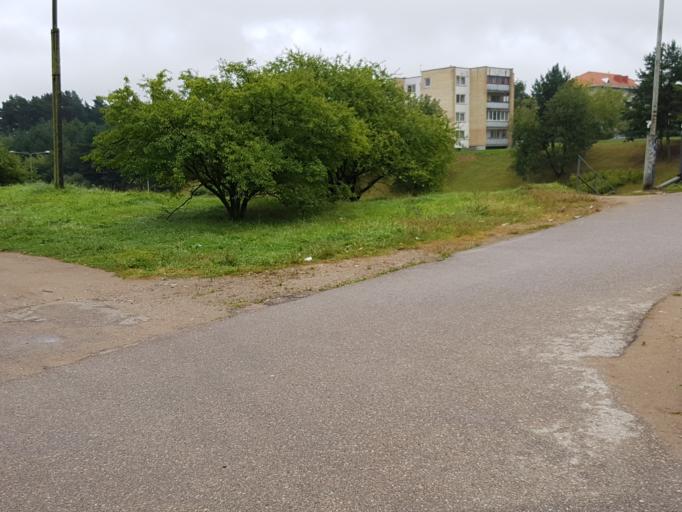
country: LT
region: Vilnius County
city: Lazdynai
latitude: 54.6715
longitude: 25.2148
